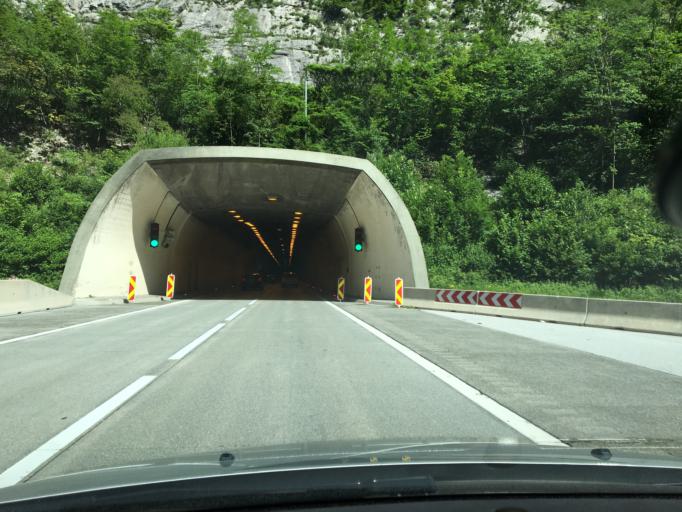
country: AT
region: Salzburg
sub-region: Politischer Bezirk Hallein
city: Golling an der Salzach
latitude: 47.5661
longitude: 13.1723
